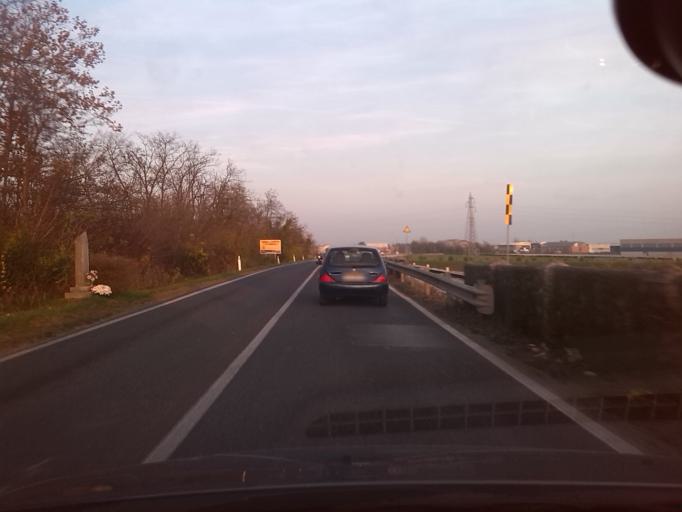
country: IT
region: Friuli Venezia Giulia
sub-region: Provincia di Udine
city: Remanzacco
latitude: 46.0773
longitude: 13.2925
